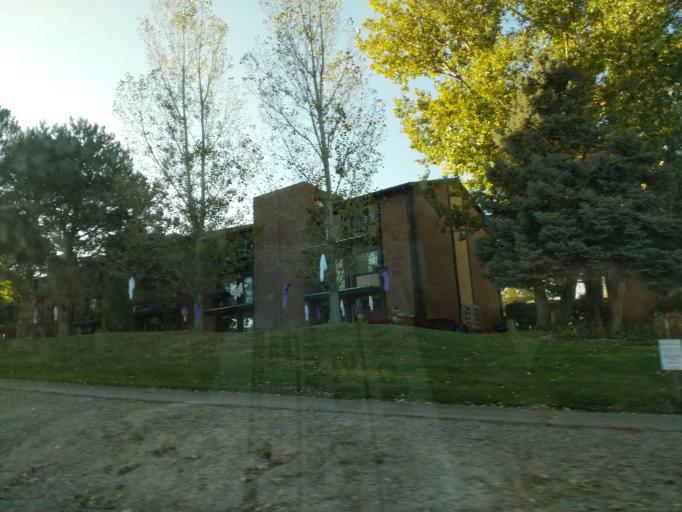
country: US
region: Colorado
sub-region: Mesa County
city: Redlands
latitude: 39.0587
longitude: -108.6108
